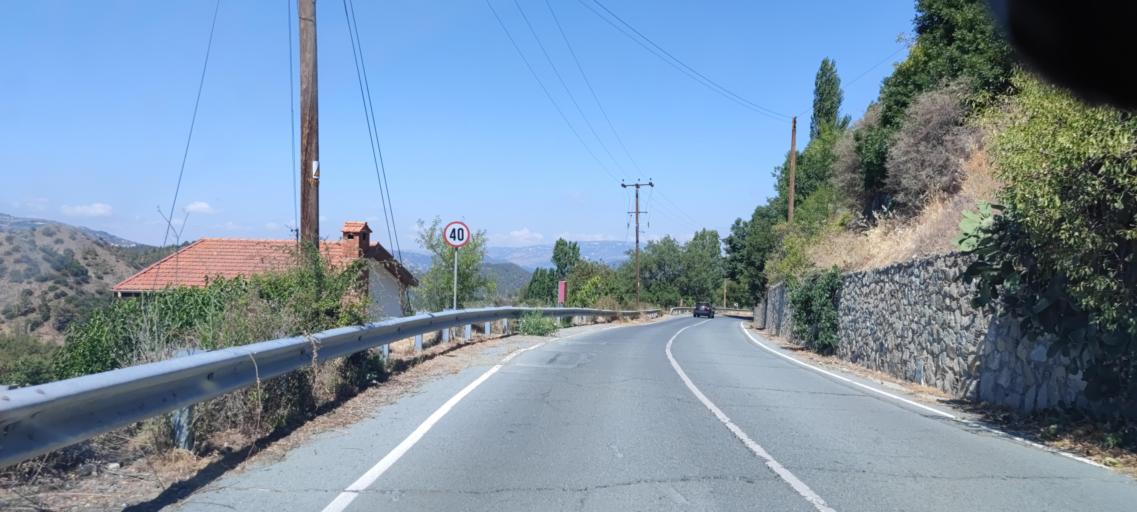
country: CY
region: Lefkosia
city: Kakopetria
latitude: 34.8949
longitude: 32.8291
